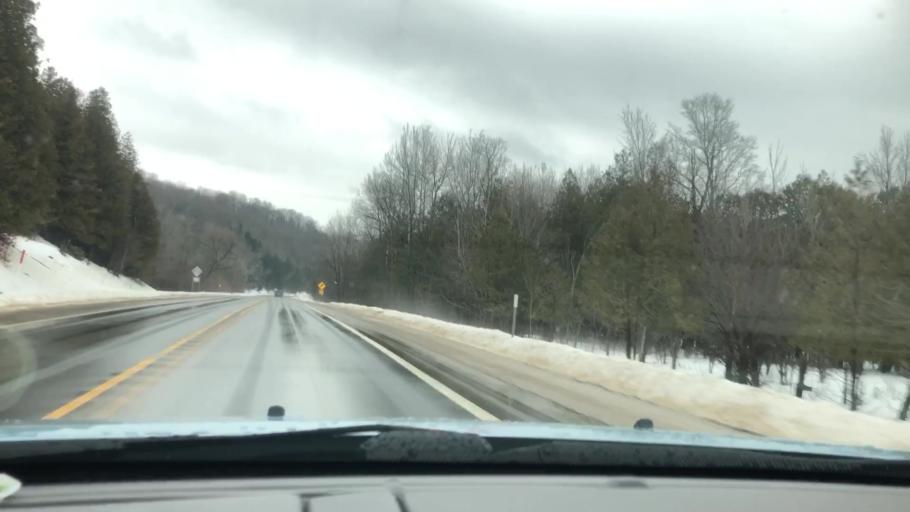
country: US
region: Michigan
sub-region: Charlevoix County
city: East Jordan
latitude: 45.1287
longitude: -85.0784
